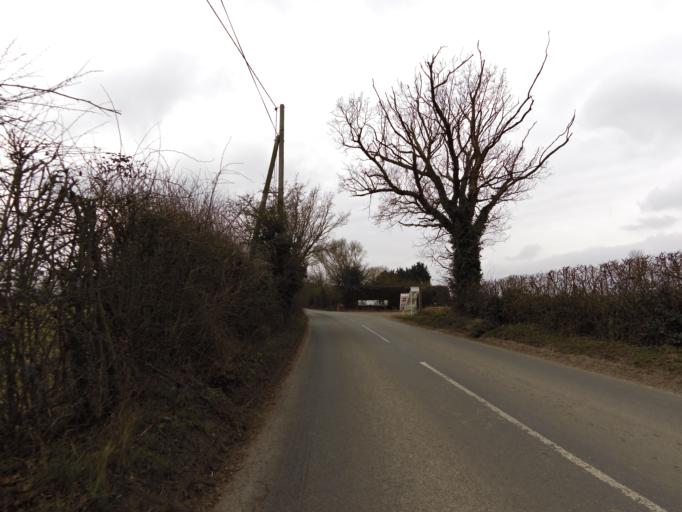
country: GB
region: England
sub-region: Suffolk
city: Halesworth
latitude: 52.4018
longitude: 1.5223
